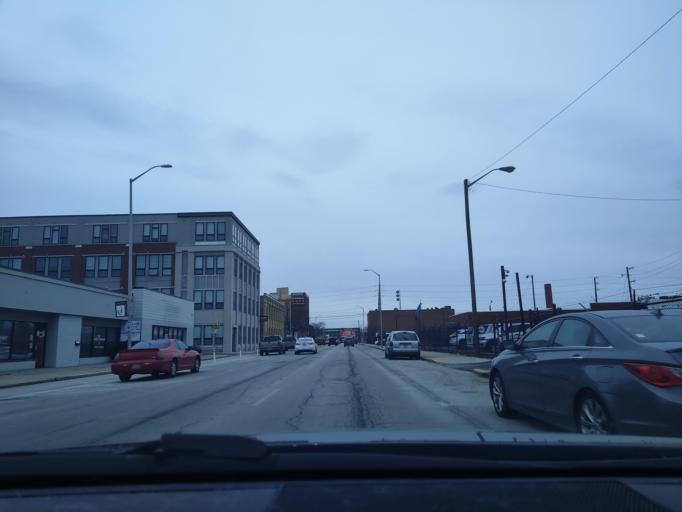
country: US
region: Indiana
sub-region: Marion County
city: Indianapolis
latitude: 39.7848
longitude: -86.1594
